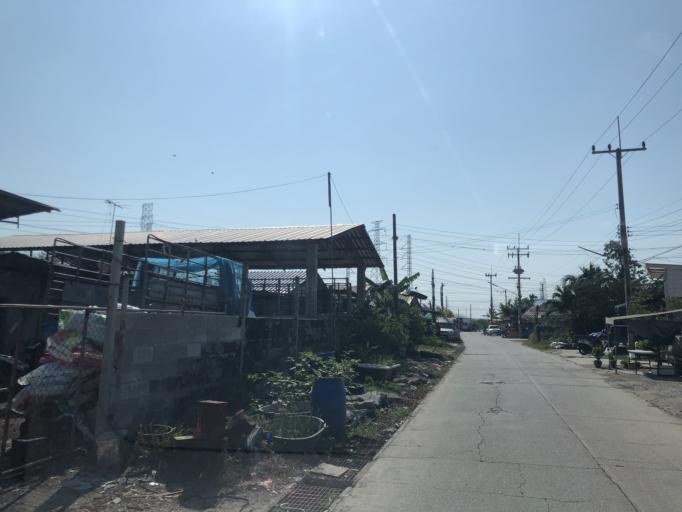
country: TH
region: Chachoengsao
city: Bang Pakong
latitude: 13.5169
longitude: 101.0225
